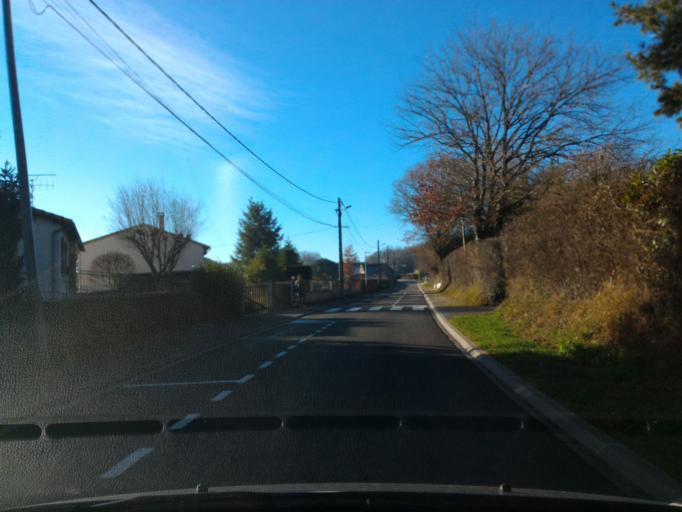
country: FR
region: Poitou-Charentes
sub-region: Departement de la Charente
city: Champagne-Mouton
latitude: 45.9885
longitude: 0.4063
